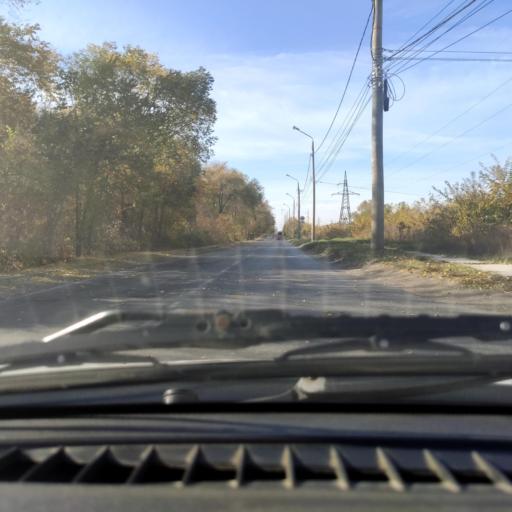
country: RU
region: Samara
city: Zhigulevsk
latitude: 53.4633
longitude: 49.5652
